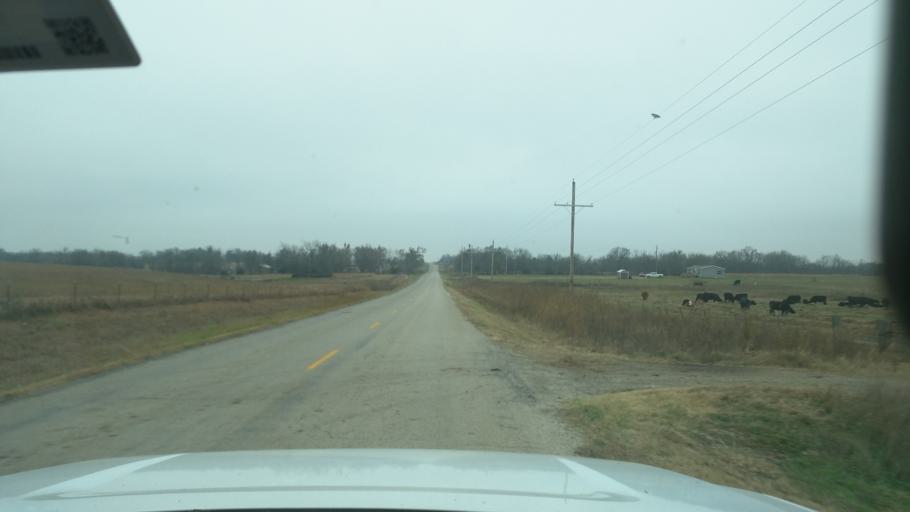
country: US
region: Kansas
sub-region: Morris County
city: Council Grove
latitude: 38.6298
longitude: -96.2614
